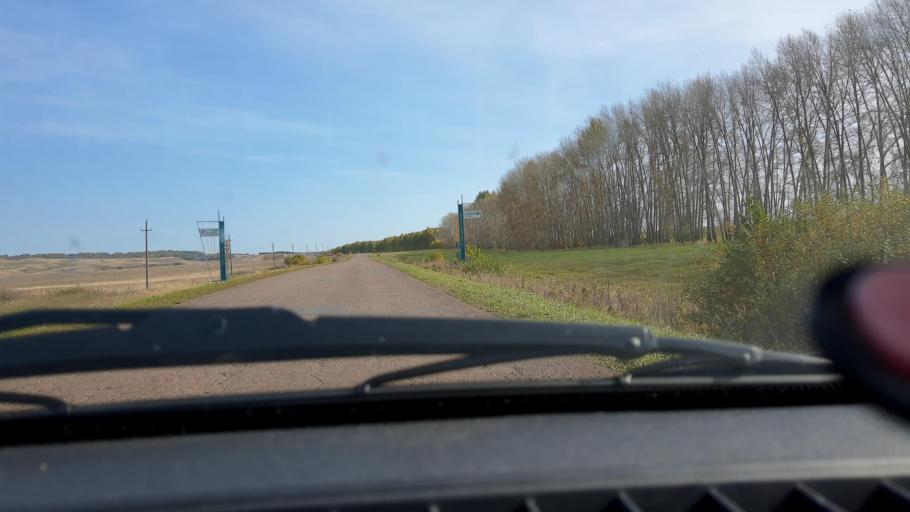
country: RU
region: Bashkortostan
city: Chekmagush
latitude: 54.8883
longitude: 54.5815
